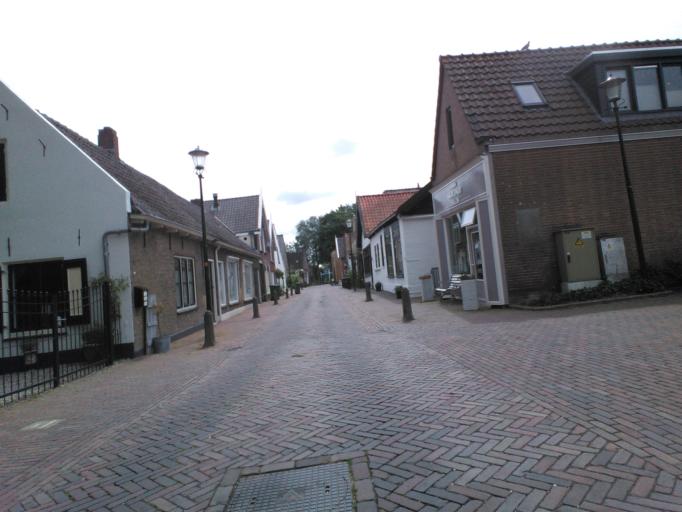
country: NL
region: South Holland
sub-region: Molenwaard
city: Nieuw-Lekkerland
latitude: 51.9452
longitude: 4.7091
